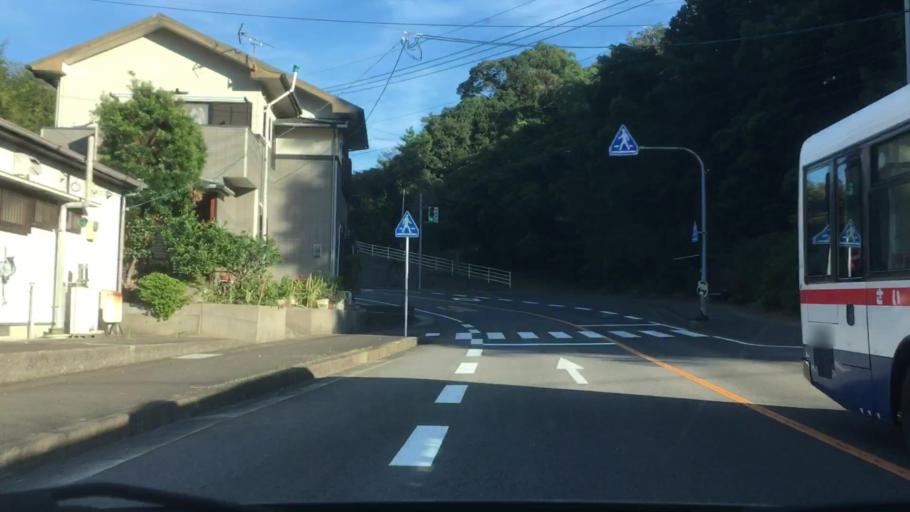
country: JP
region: Nagasaki
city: Sasebo
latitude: 33.0345
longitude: 129.6099
